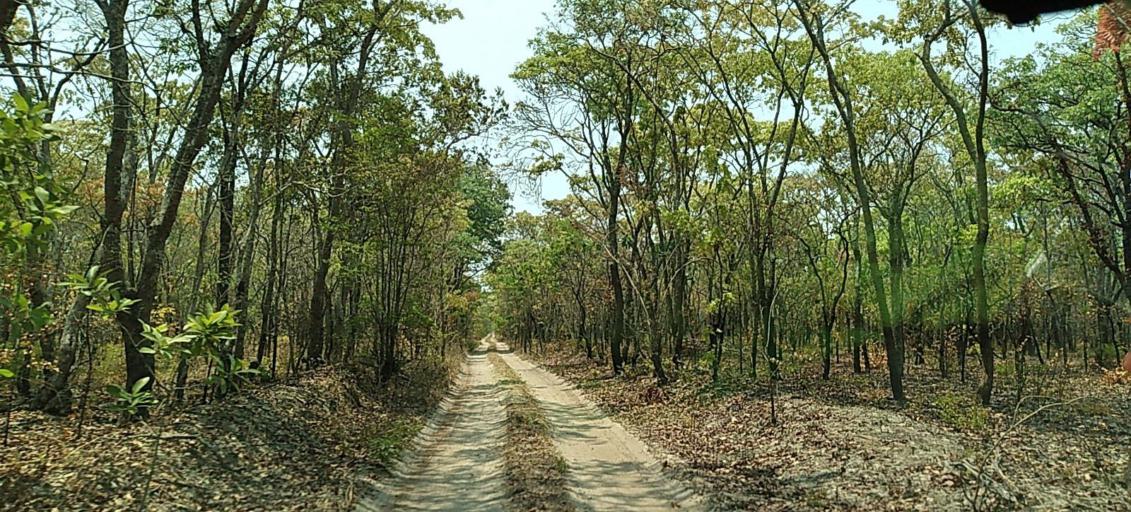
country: ZM
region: North-Western
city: Kabompo
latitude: -13.6554
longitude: 24.4658
